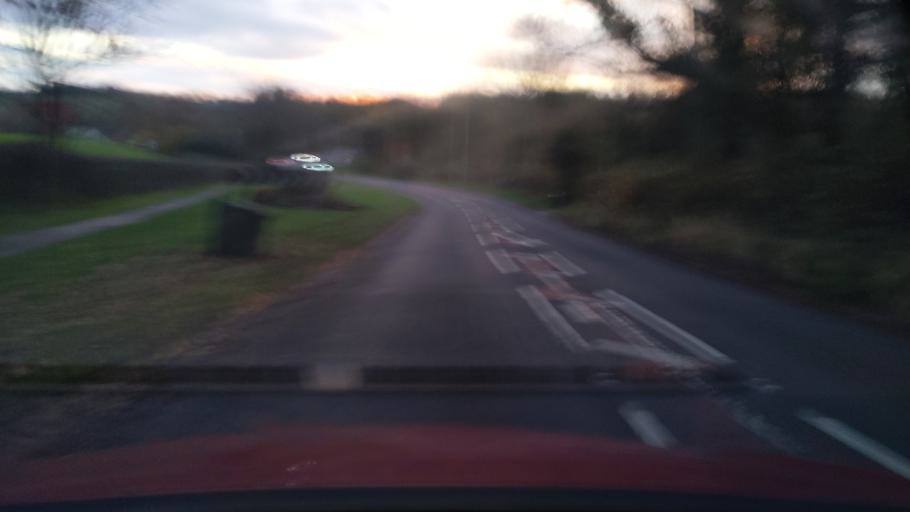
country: GB
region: England
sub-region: Lancashire
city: Clayton-le-Woods
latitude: 53.7013
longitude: -2.6524
